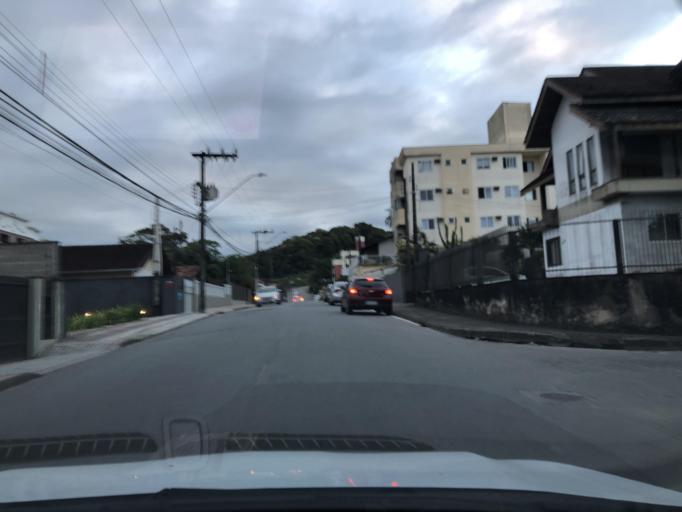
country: BR
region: Santa Catarina
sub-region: Joinville
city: Joinville
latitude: -26.2911
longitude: -48.8763
